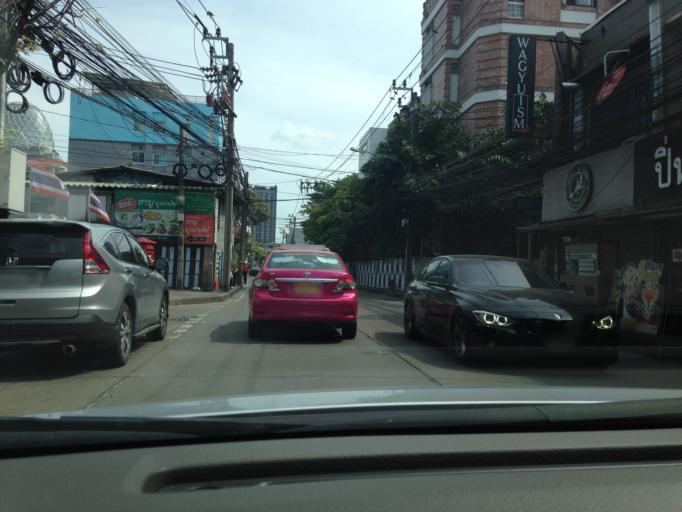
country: TH
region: Bangkok
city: Phaya Thai
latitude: 13.7793
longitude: 100.5375
